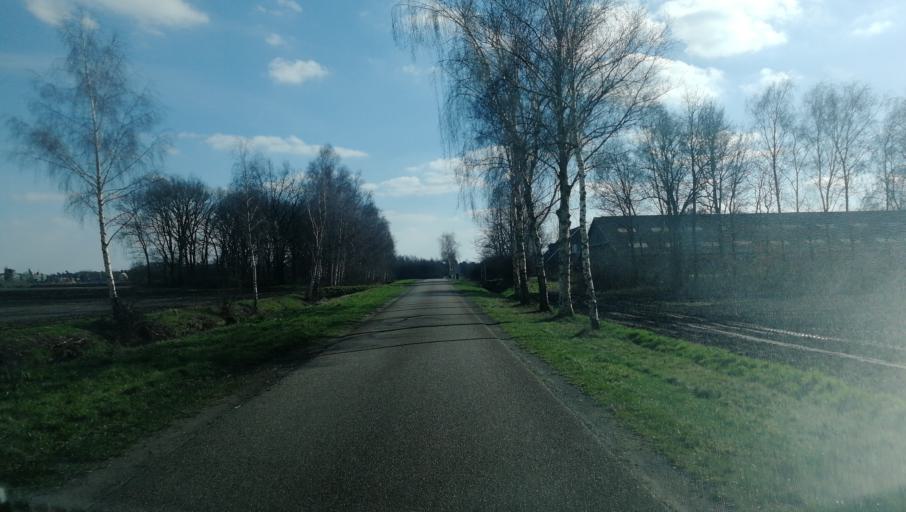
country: NL
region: Limburg
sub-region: Gemeente Peel en Maas
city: Maasbree
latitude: 51.4022
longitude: 5.9738
